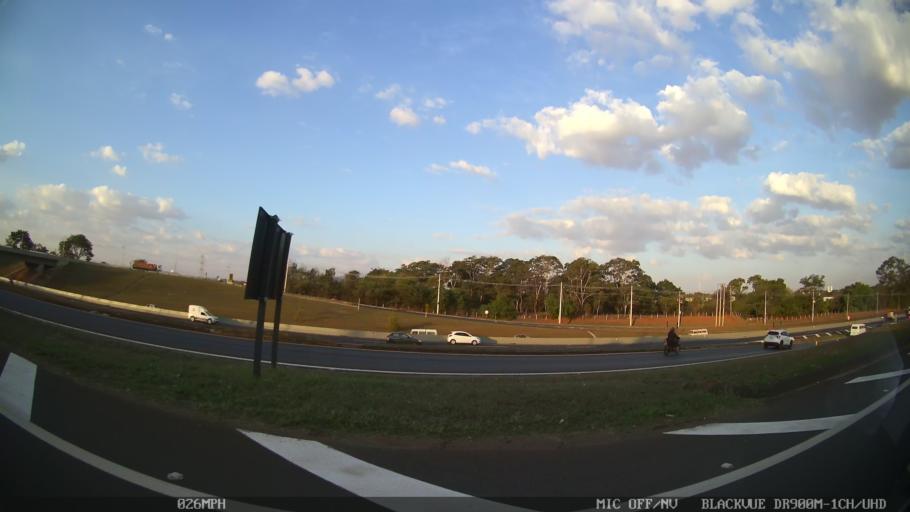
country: BR
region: Sao Paulo
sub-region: Ribeirao Preto
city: Ribeirao Preto
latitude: -21.1508
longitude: -47.7583
